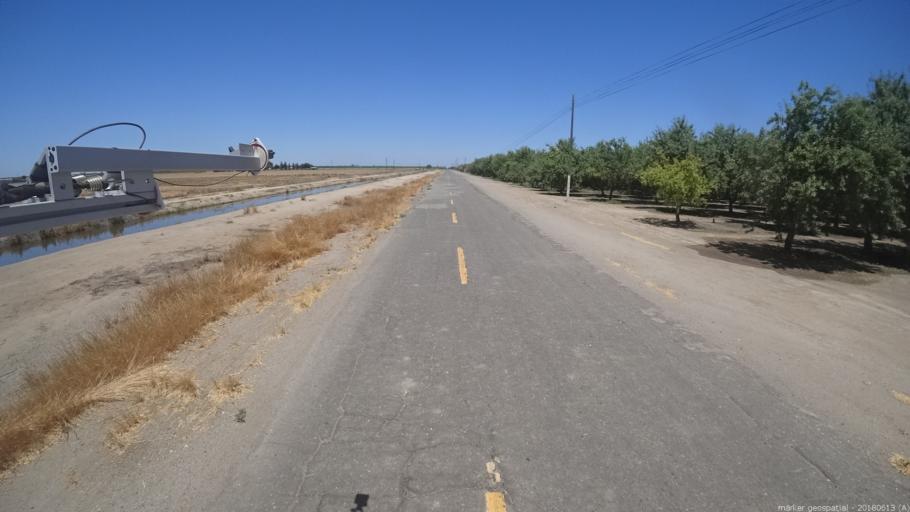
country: US
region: California
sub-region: Madera County
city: Chowchilla
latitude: 37.0151
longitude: -120.2924
